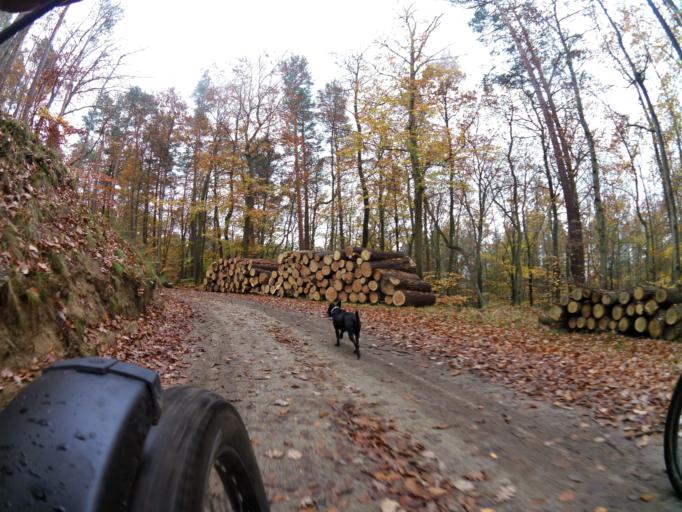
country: PL
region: Pomeranian Voivodeship
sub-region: Powiat pucki
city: Krokowa
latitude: 54.7475
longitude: 18.0915
